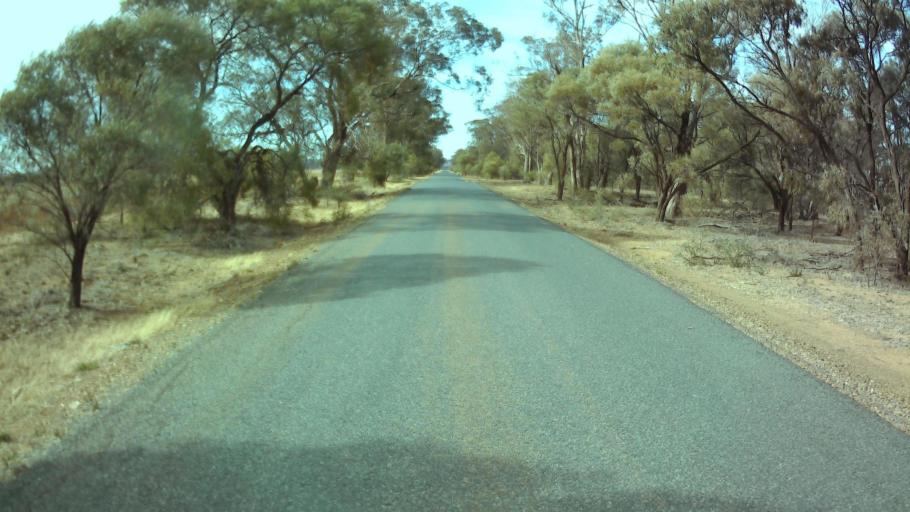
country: AU
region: New South Wales
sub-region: Weddin
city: Grenfell
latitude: -33.8695
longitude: 147.8583
